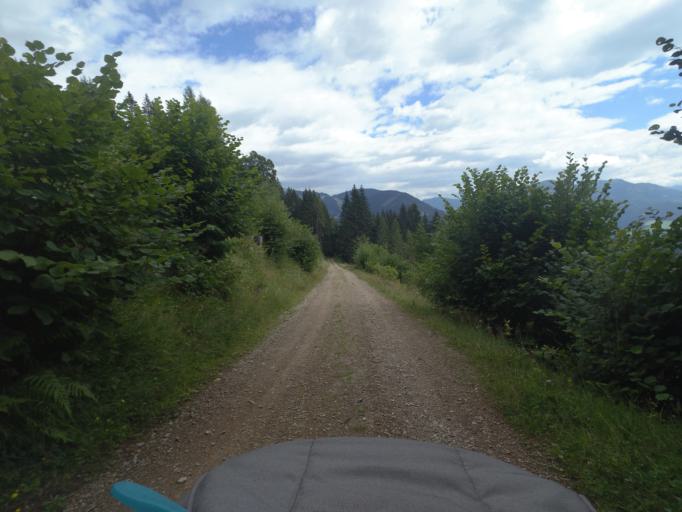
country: AT
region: Salzburg
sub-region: Politischer Bezirk Sankt Johann im Pongau
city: Werfenweng
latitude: 47.4734
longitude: 13.2320
